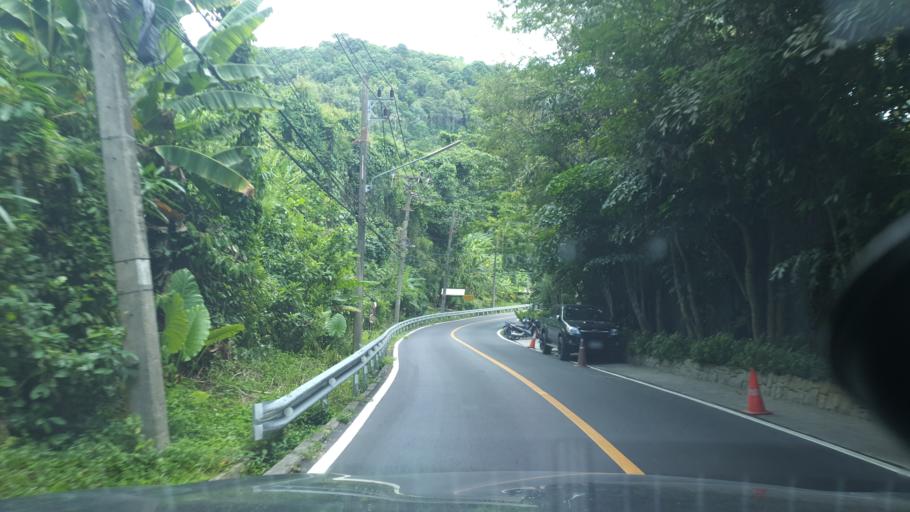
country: TH
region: Phuket
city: Thalang
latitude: 8.0487
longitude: 98.2779
